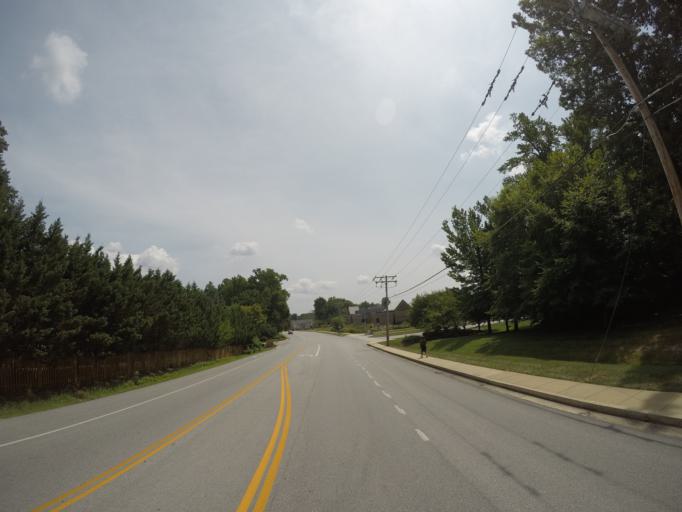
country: US
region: Maryland
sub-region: Howard County
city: Savage
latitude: 39.1329
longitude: -76.8379
